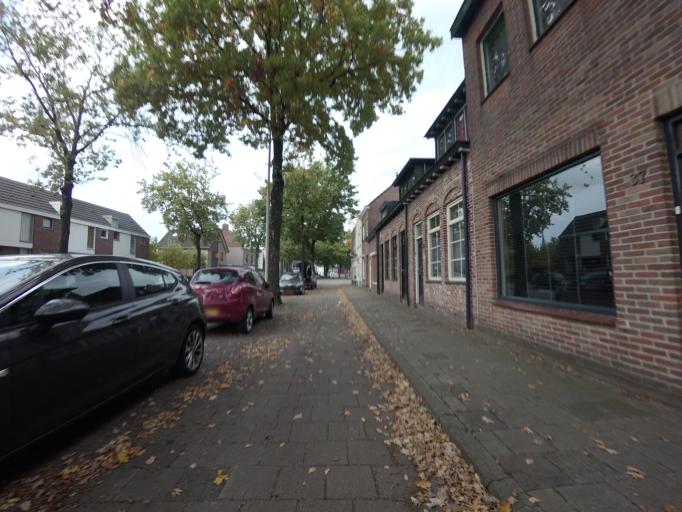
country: NL
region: North Brabant
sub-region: Gemeente Breda
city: Breda
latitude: 51.5729
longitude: 4.7434
